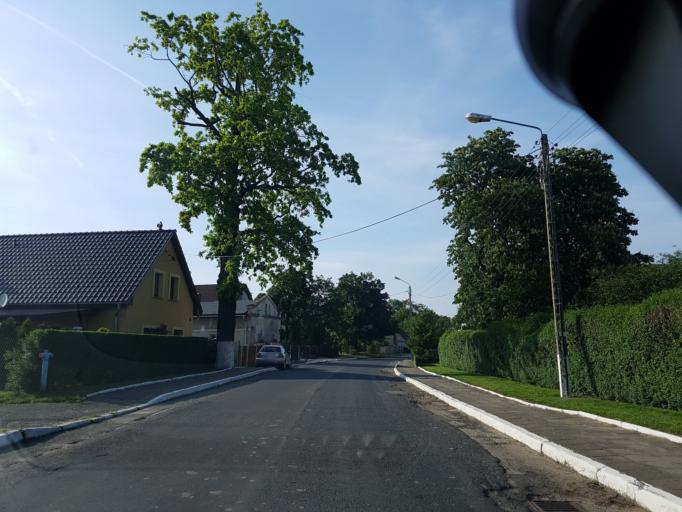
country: PL
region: Lower Silesian Voivodeship
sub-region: Powiat strzelinski
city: Wiazow
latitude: 50.8525
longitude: 17.1857
